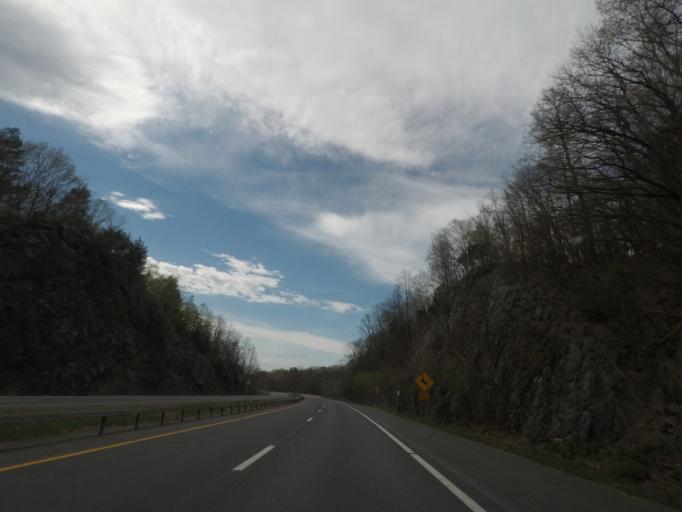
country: US
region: New York
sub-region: Greene County
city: Jefferson Heights
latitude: 42.2474
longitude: -73.8942
